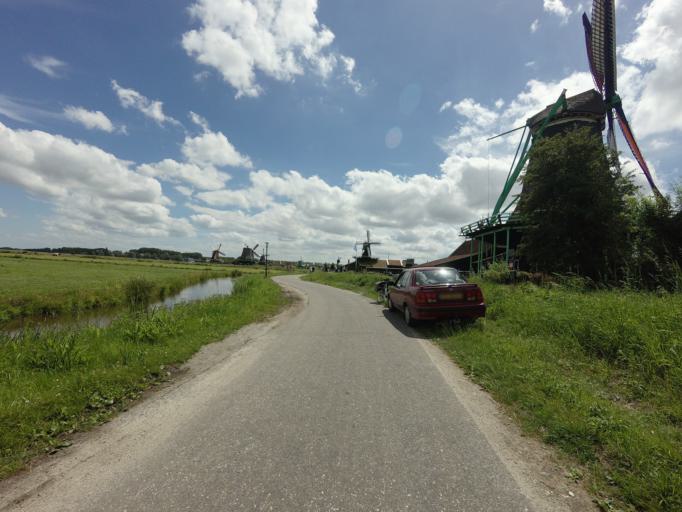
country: NL
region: North Holland
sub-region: Gemeente Zaanstad
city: Zaanstad
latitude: 52.4784
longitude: 4.8134
